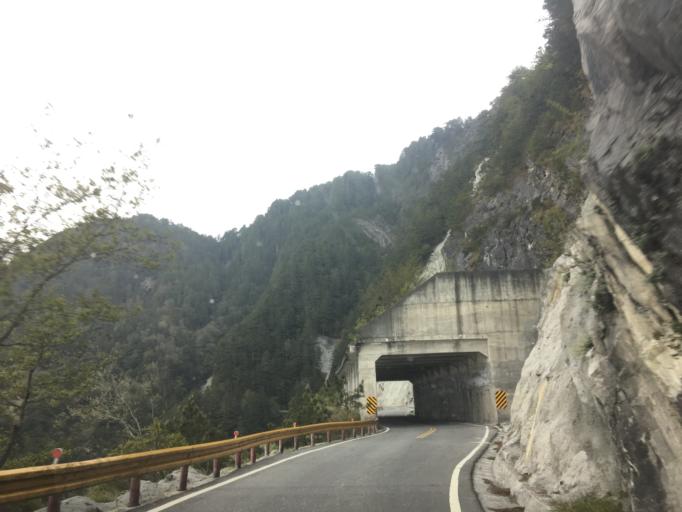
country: TW
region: Taiwan
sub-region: Hualien
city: Hualian
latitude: 24.1743
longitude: 121.3781
